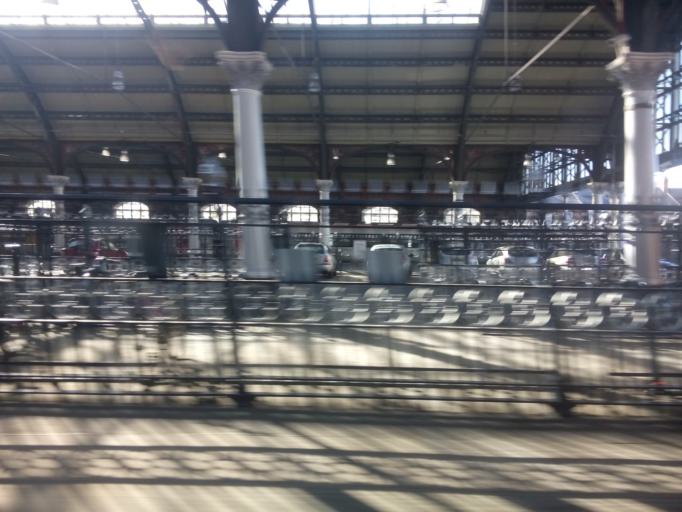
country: GB
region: England
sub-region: Darlington
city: Darlington
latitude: 54.5222
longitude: -1.5459
